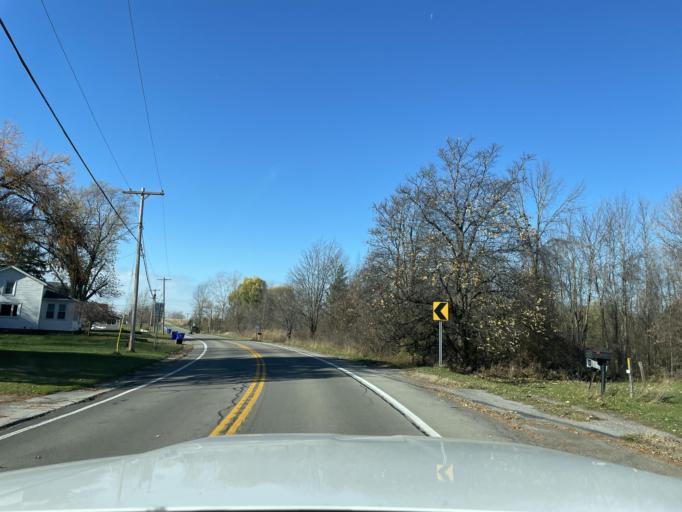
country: US
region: New York
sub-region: Niagara County
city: Middleport
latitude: 43.2159
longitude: -78.4452
